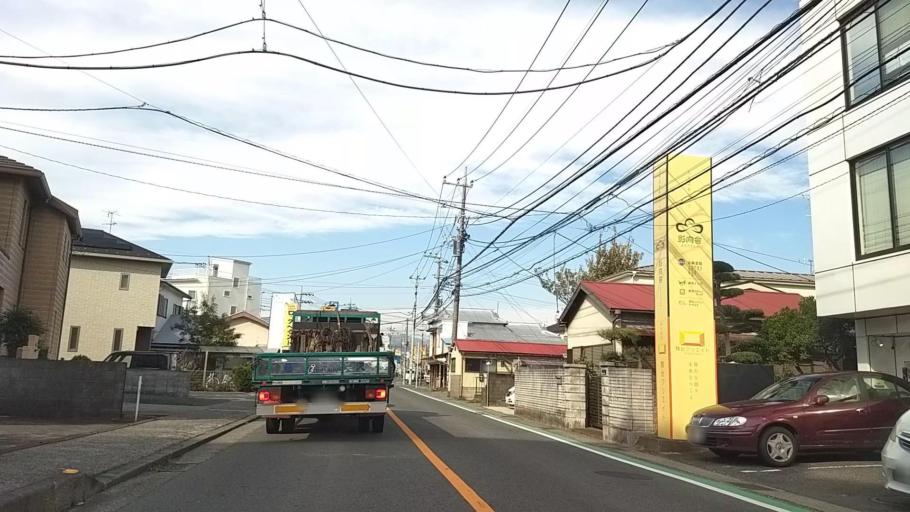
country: JP
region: Kanagawa
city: Atsugi
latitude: 35.4484
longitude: 139.3621
